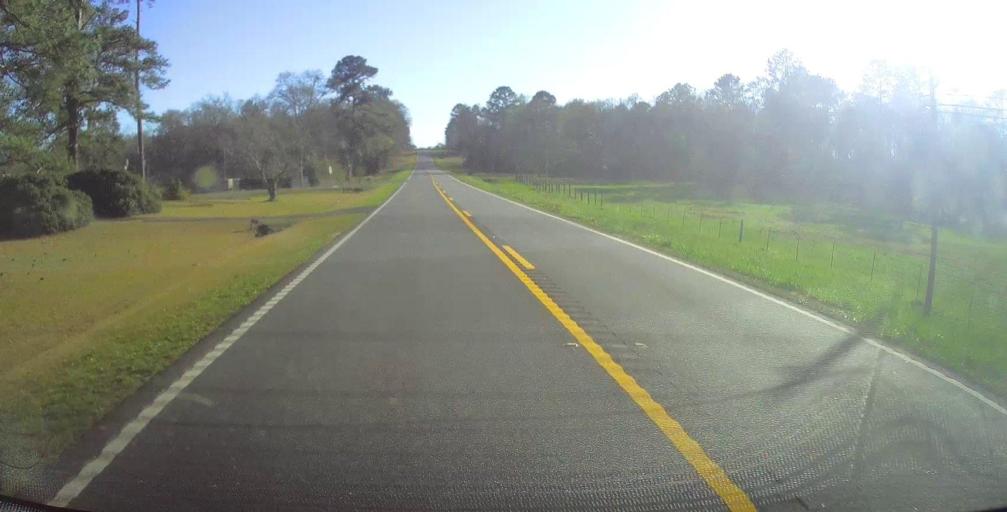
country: US
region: Georgia
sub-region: Taylor County
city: Reynolds
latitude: 32.5523
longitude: -84.0973
